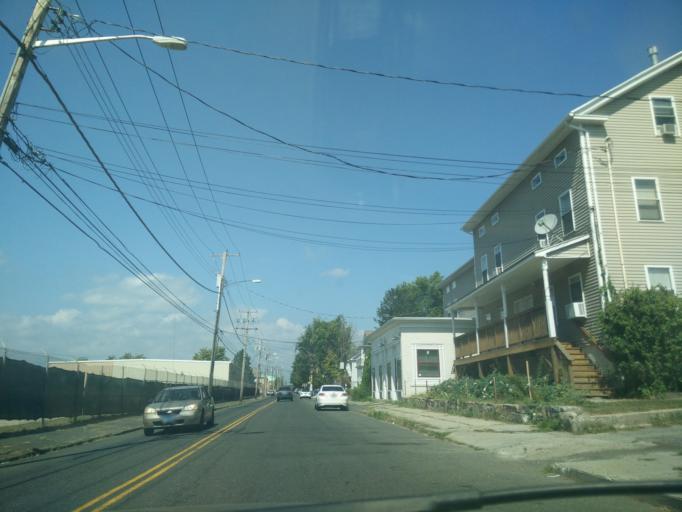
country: US
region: Connecticut
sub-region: Fairfield County
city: Stratford
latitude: 41.1875
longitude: -73.1701
